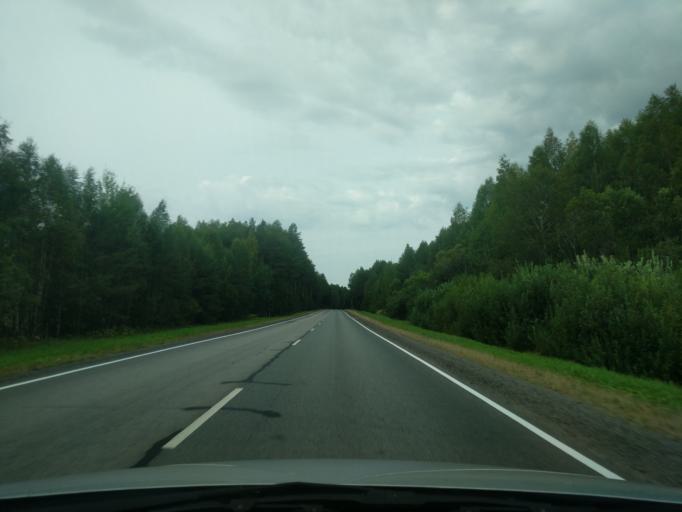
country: RU
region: Kirov
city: Svecha
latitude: 58.2715
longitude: 47.7297
